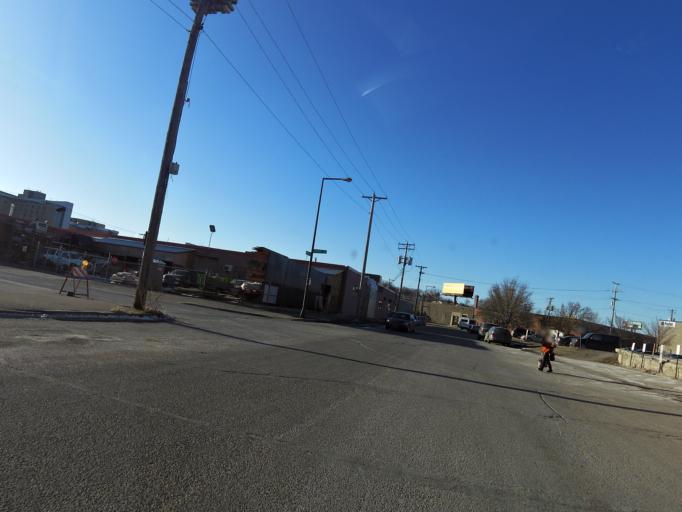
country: US
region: Minnesota
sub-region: Ramsey County
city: Saint Paul
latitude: 44.9547
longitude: -93.0883
